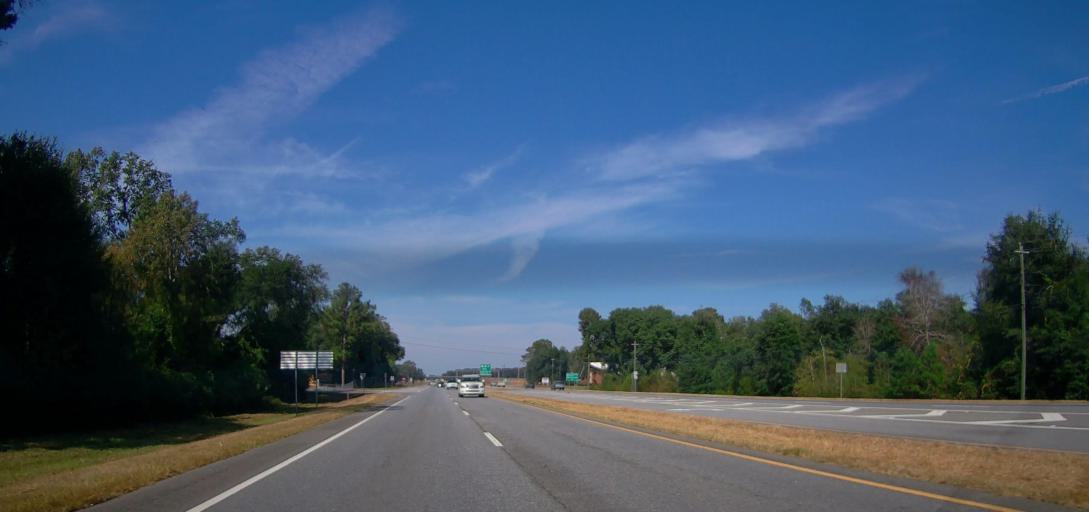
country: US
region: Georgia
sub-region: Dougherty County
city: Albany
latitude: 31.5379
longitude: -84.1154
